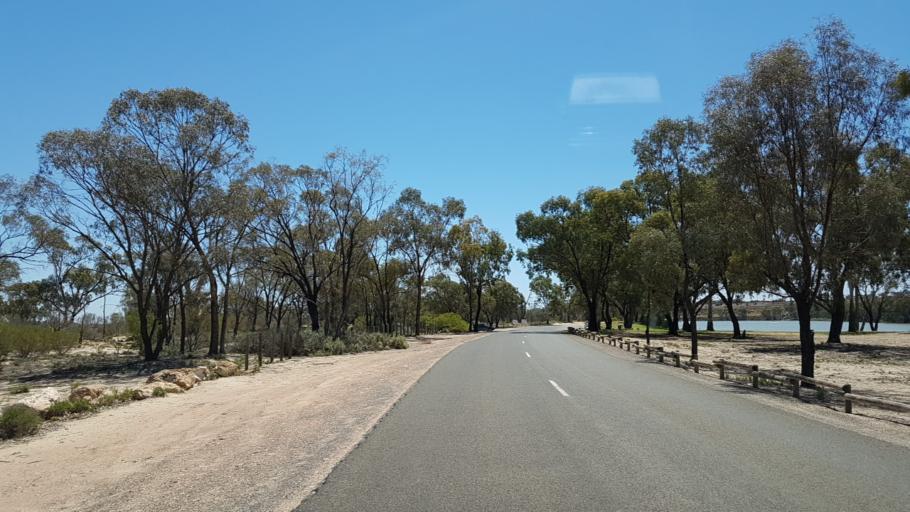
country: AU
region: South Australia
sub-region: Loxton Waikerie
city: Waikerie
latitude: -34.1699
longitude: 139.9763
